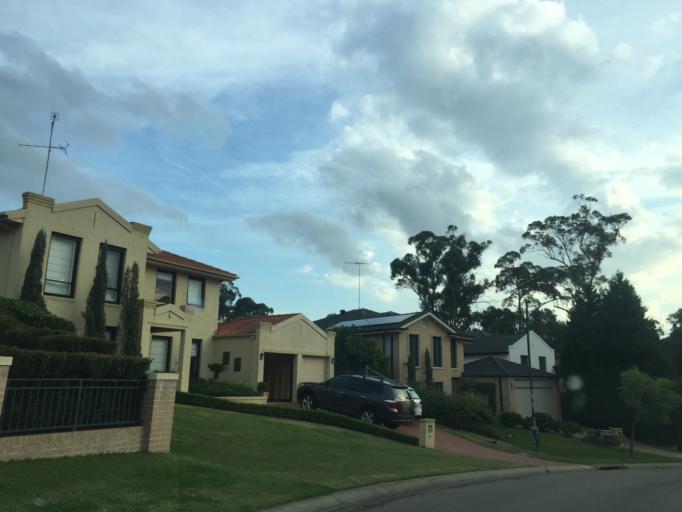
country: AU
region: New South Wales
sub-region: The Hills Shire
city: Glenhaven
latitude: -33.7020
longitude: 150.9765
